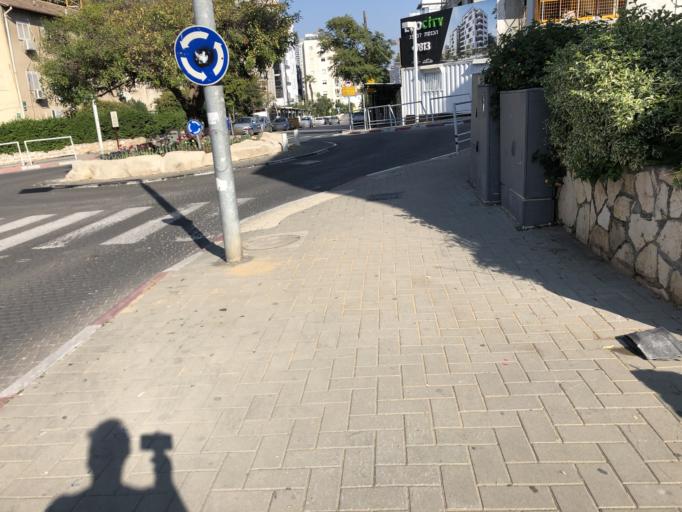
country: IL
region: Tel Aviv
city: Giv`atayim
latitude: 32.0690
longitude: 34.8124
